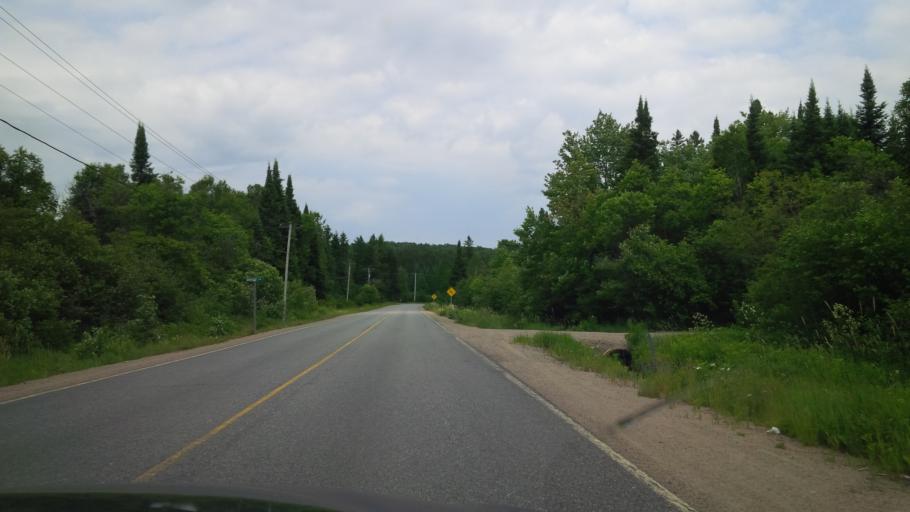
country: CA
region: Ontario
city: Huntsville
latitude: 45.5686
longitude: -79.2250
